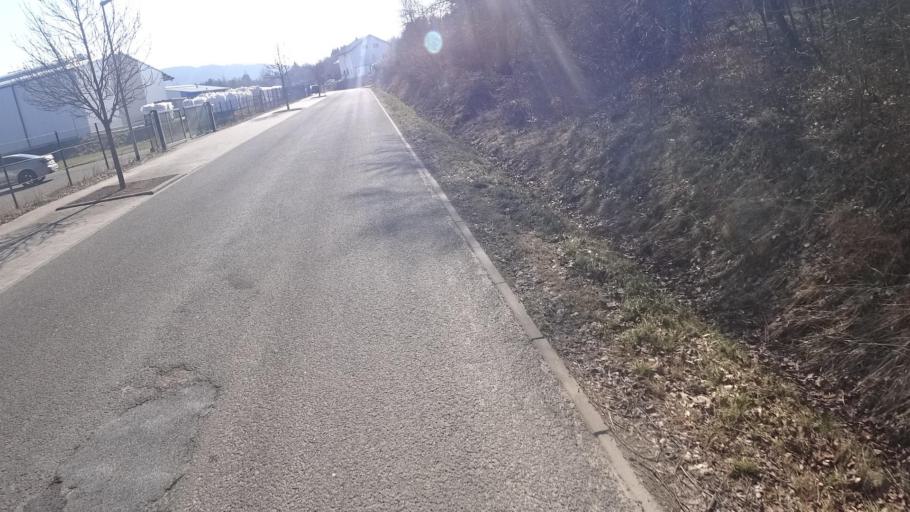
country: DE
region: Rheinland-Pfalz
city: Rheinbollen
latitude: 49.9950
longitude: 7.6812
